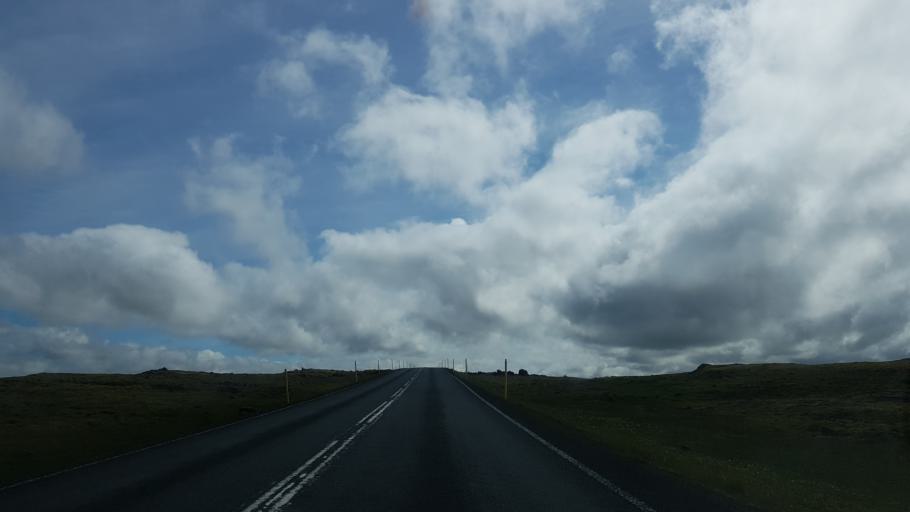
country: IS
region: West
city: Borgarnes
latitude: 64.9946
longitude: -21.0637
